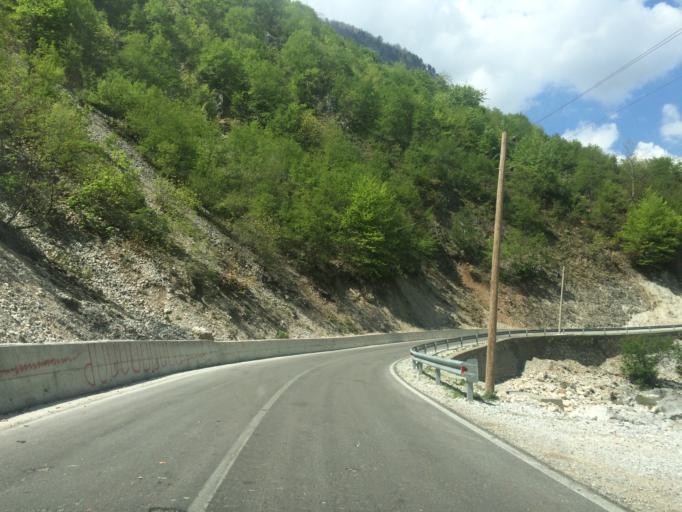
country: AL
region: Kukes
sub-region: Rrethi i Tropojes
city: Bajram Curri
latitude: 42.4166
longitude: 20.0099
